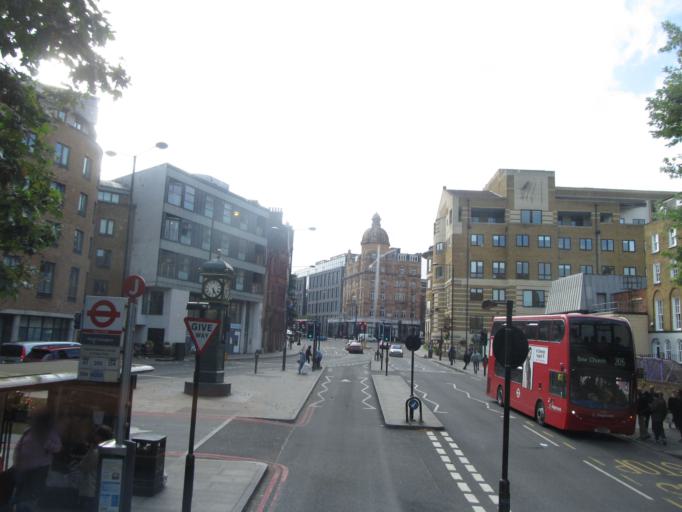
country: GB
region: England
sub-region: Greater London
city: Islington
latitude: 51.5316
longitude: -0.1048
